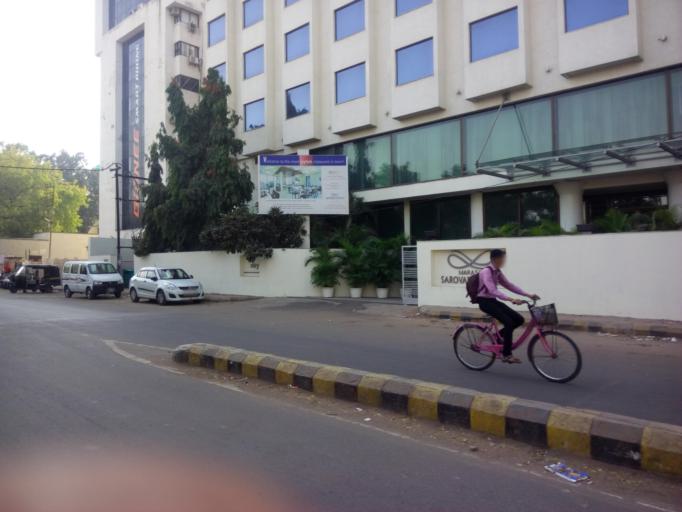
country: IN
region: Gujarat
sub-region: Rajkot
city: Rajkot
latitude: 22.2963
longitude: 70.7987
